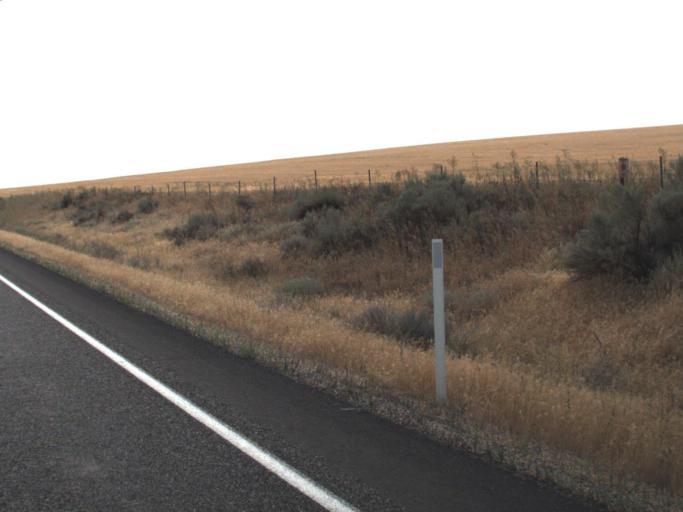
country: US
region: Washington
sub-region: Benton County
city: Prosser
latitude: 46.1972
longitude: -119.7058
